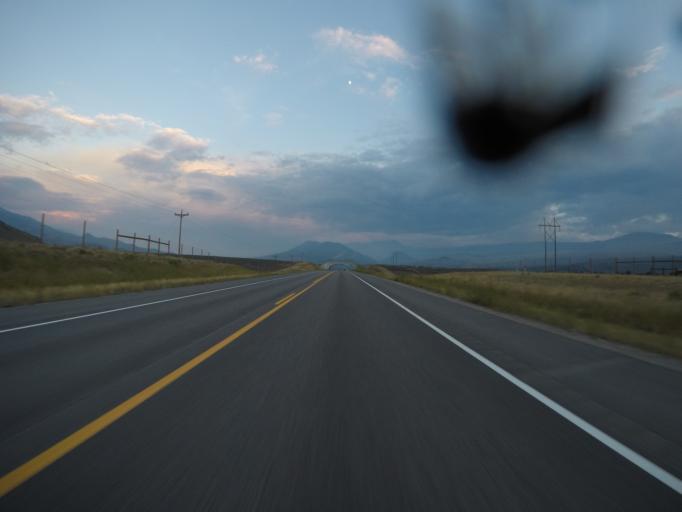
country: US
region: Colorado
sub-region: Grand County
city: Kremmling
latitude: 39.9423
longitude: -106.3452
